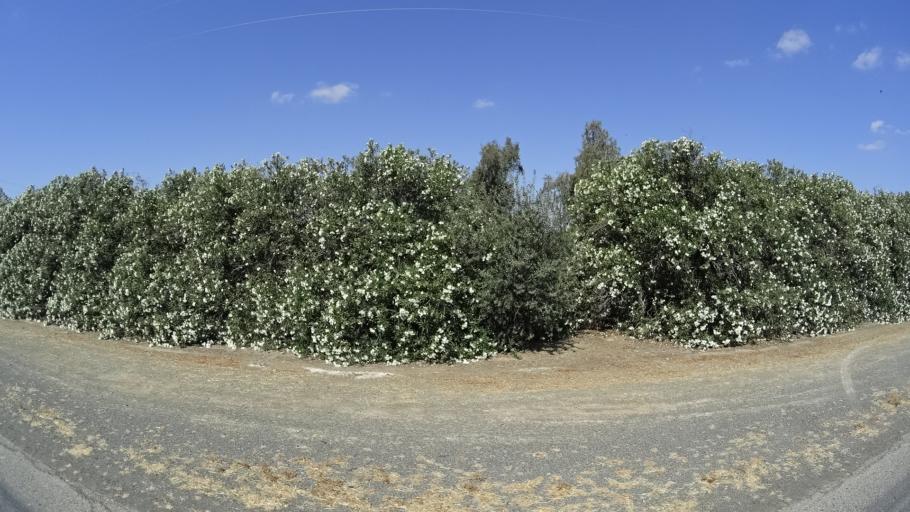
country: US
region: California
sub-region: Kings County
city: Home Garden
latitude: 36.2391
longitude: -119.6369
